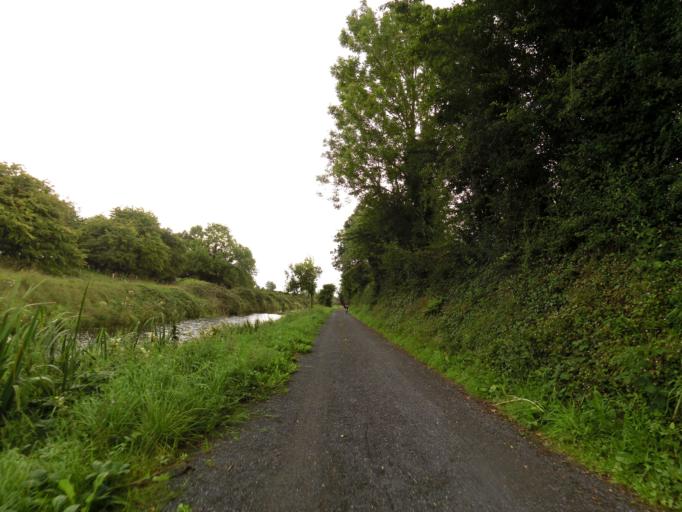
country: IE
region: Leinster
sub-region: An Iarmhi
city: An Muileann gCearr
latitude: 53.5252
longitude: -7.4464
